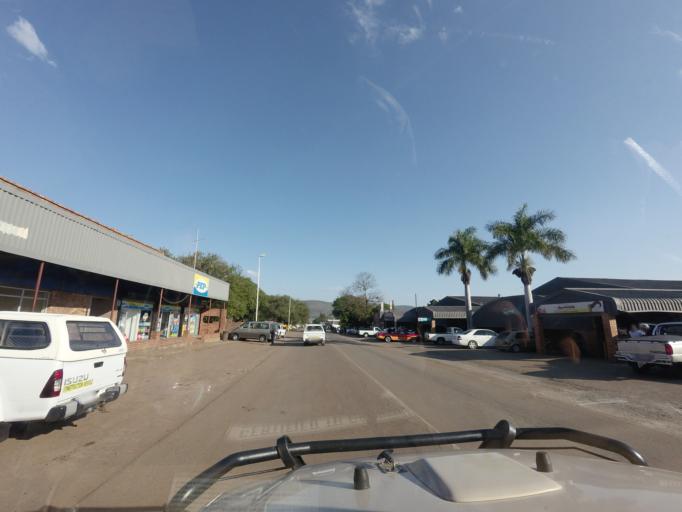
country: ZA
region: Mpumalanga
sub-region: Ehlanzeni District
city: Komatipoort
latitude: -25.4343
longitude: 31.9548
